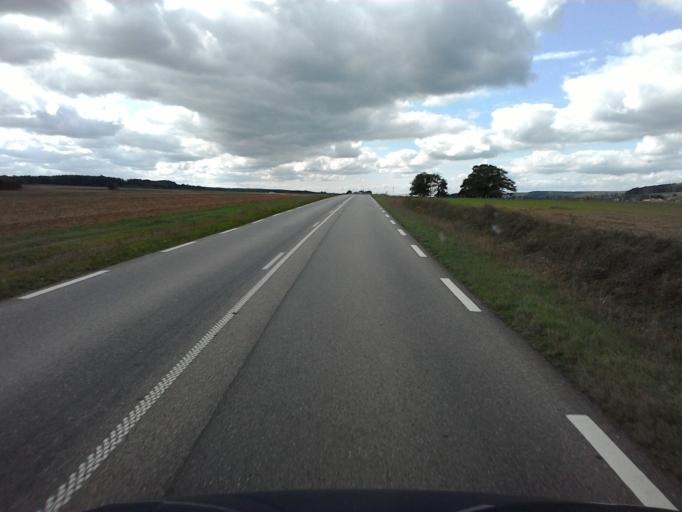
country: FR
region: Lorraine
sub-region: Departement des Vosges
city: Liffol-le-Grand
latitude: 48.3236
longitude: 5.6311
